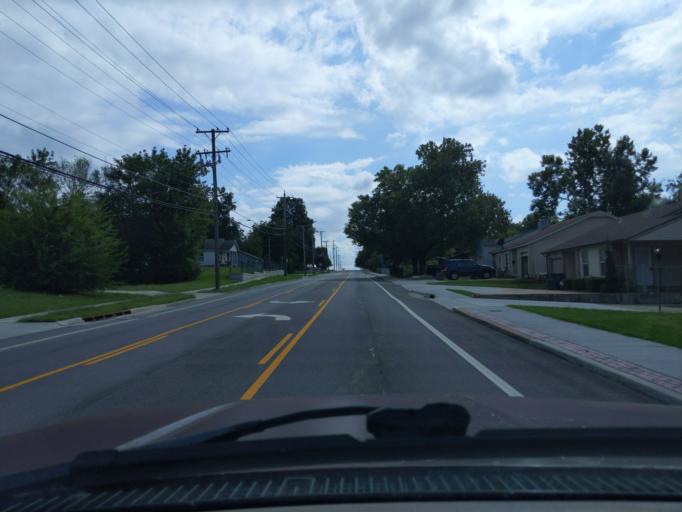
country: US
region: Oklahoma
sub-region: Tulsa County
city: Oakhurst
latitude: 36.0980
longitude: -96.0117
